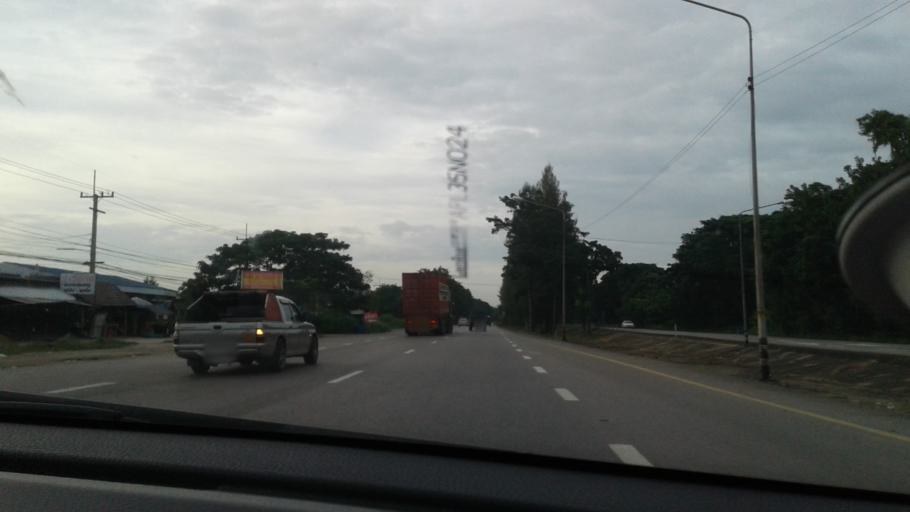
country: TH
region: Prachuap Khiri Khan
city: Pran Buri
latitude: 12.4280
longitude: 99.9178
